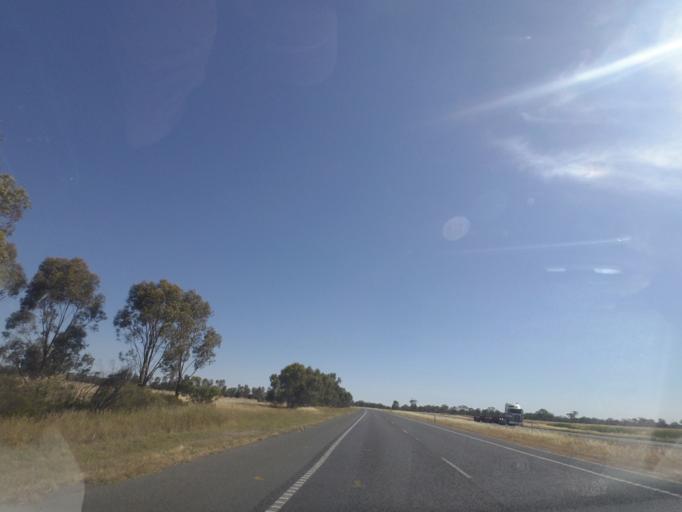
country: AU
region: Victoria
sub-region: Greater Shepparton
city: Shepparton
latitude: -36.6344
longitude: 145.2926
